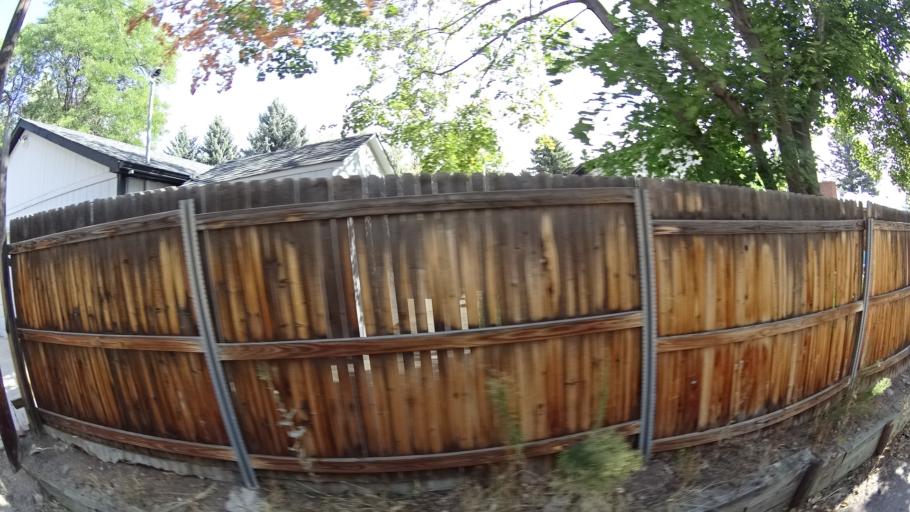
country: US
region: Colorado
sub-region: El Paso County
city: Colorado Springs
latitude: 38.8662
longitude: -104.7682
